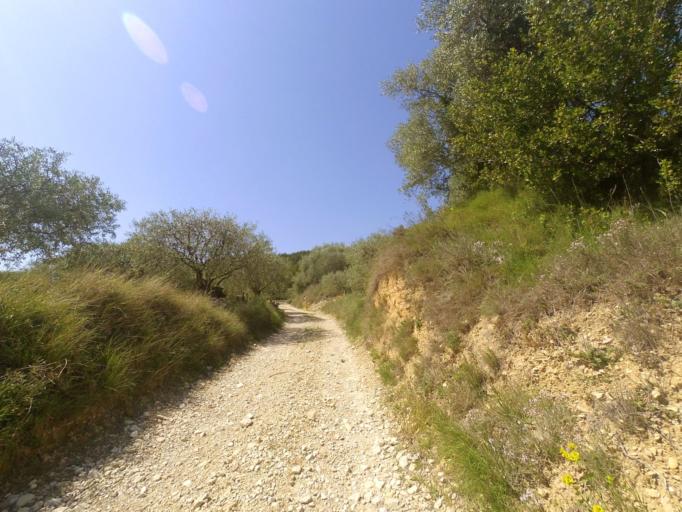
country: FR
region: Languedoc-Roussillon
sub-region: Departement du Gard
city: Calvisson
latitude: 43.7790
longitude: 4.1816
